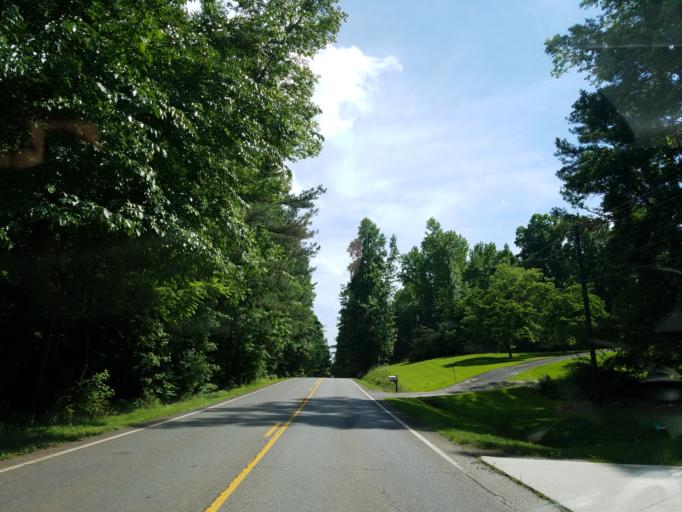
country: US
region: Georgia
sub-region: Cherokee County
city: Holly Springs
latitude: 34.1642
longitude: -84.5062
